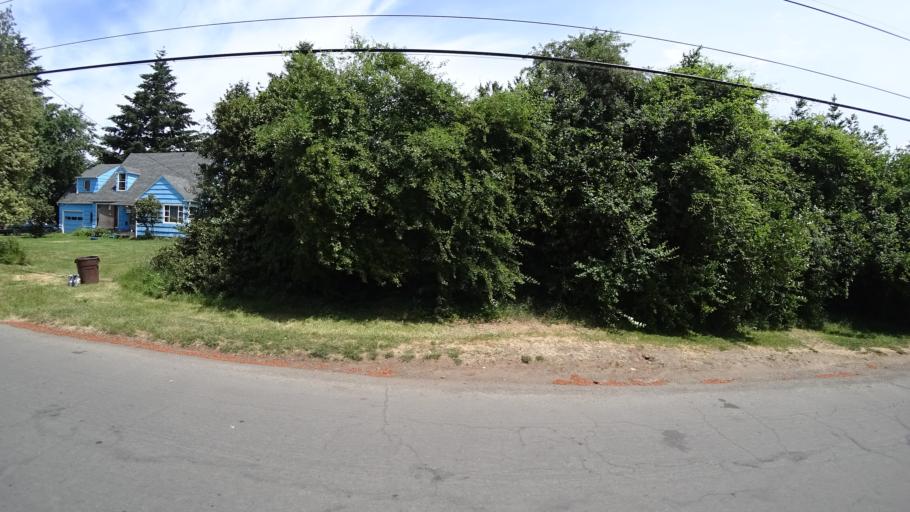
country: US
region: Oregon
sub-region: Multnomah County
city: Lents
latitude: 45.4725
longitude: -122.5992
